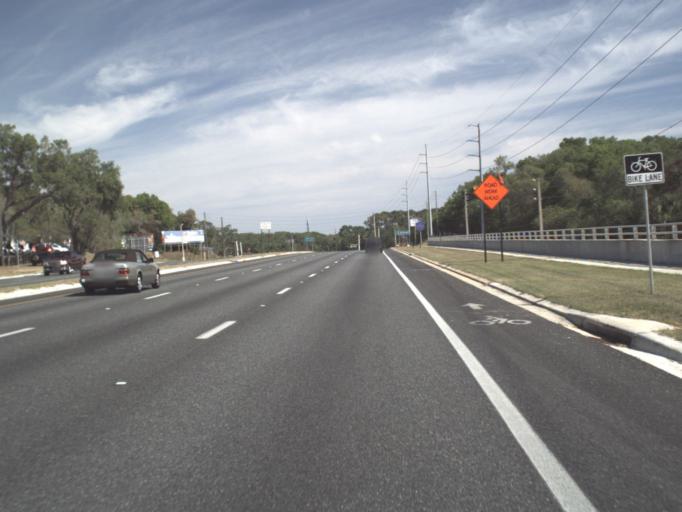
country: US
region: Florida
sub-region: Lake County
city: Fruitland Park
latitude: 28.8581
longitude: -81.9033
